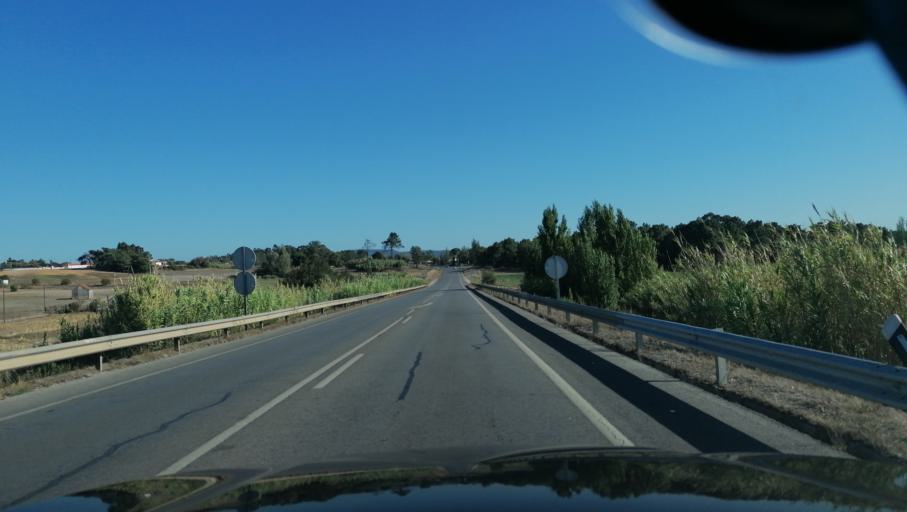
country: PT
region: Setubal
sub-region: Moita
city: Moita
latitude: 38.6393
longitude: -8.9715
